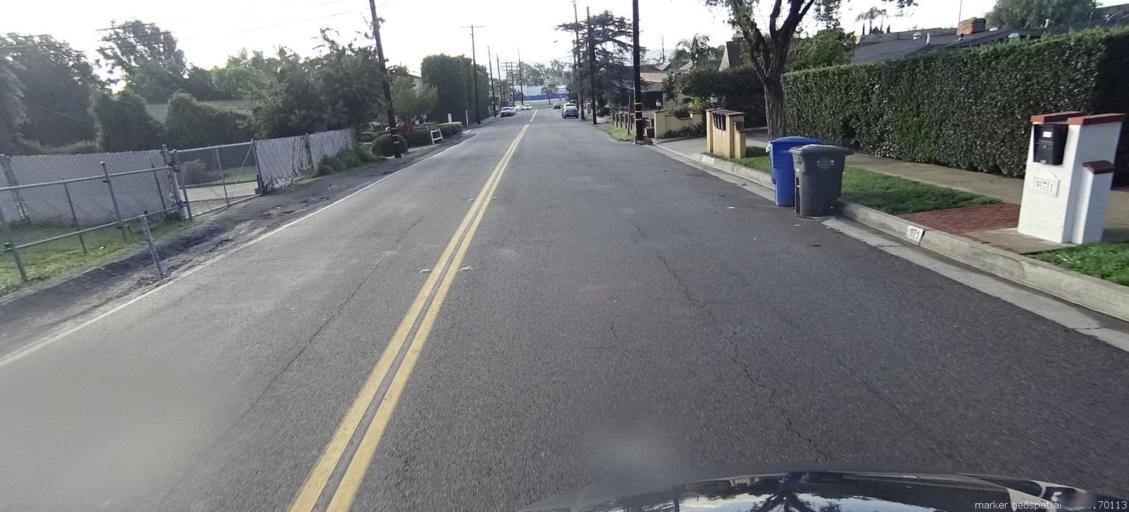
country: US
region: California
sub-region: Orange County
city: La Habra
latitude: 33.9413
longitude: -117.9571
